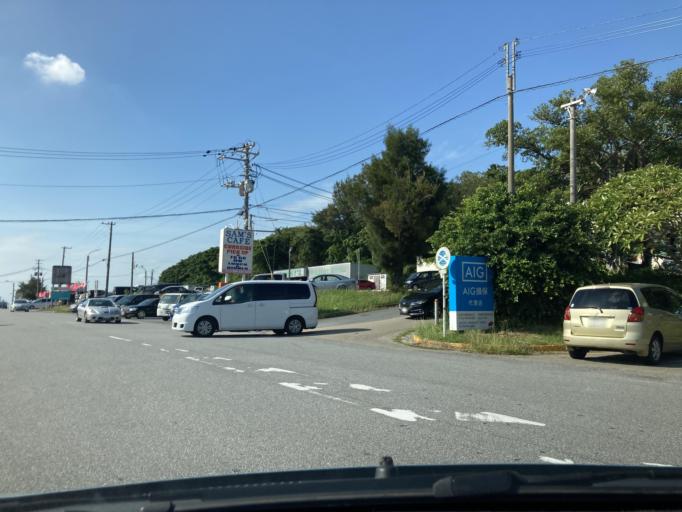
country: JP
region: Okinawa
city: Chatan
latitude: 26.2968
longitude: 127.7794
